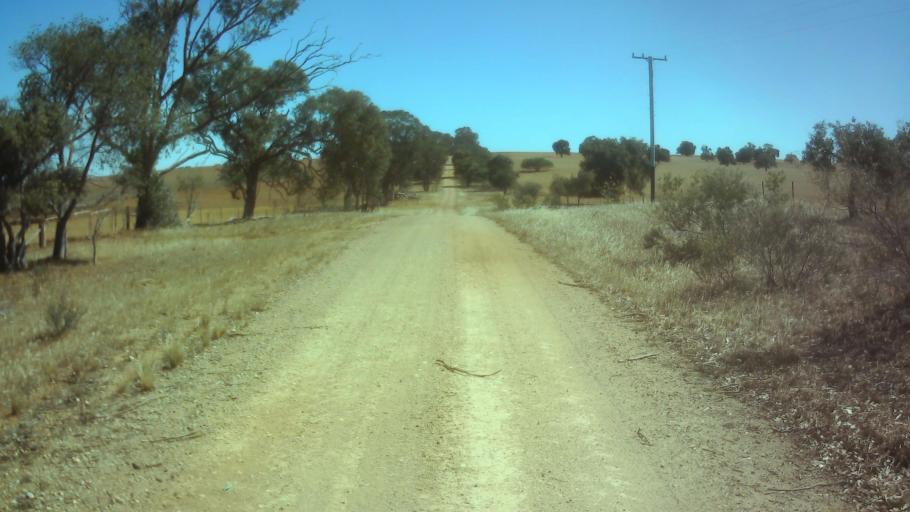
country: AU
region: New South Wales
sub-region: Weddin
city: Grenfell
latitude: -33.9819
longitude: 148.3417
